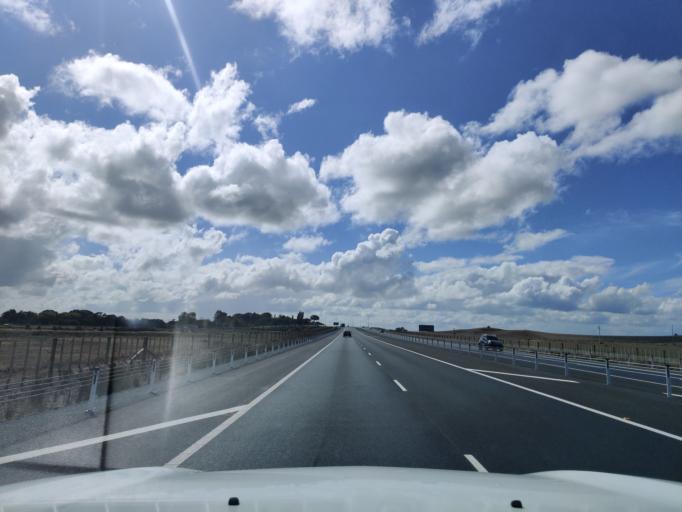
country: NZ
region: Waikato
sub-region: Waikato District
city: Te Kauwhata
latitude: -37.5148
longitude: 175.1697
